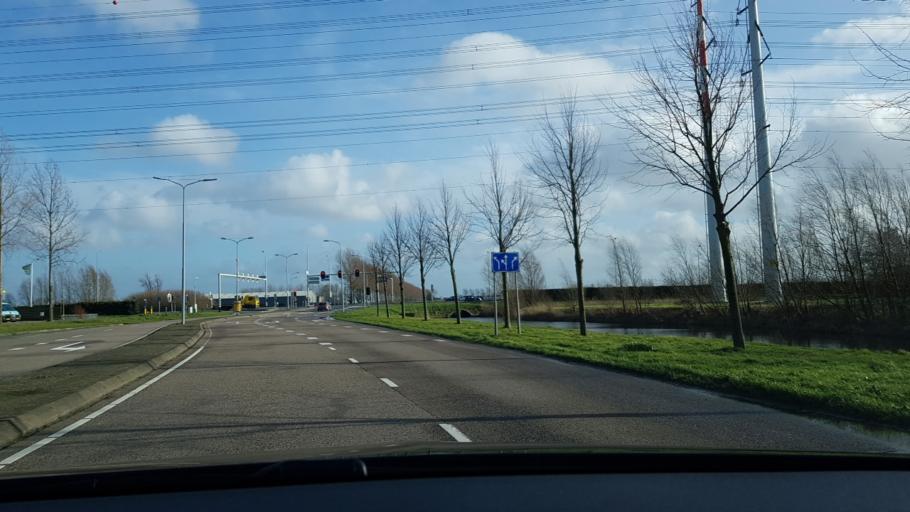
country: NL
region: North Holland
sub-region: Gemeente Haarlemmermeer
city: Hoofddorp
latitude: 52.3453
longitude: 4.6852
